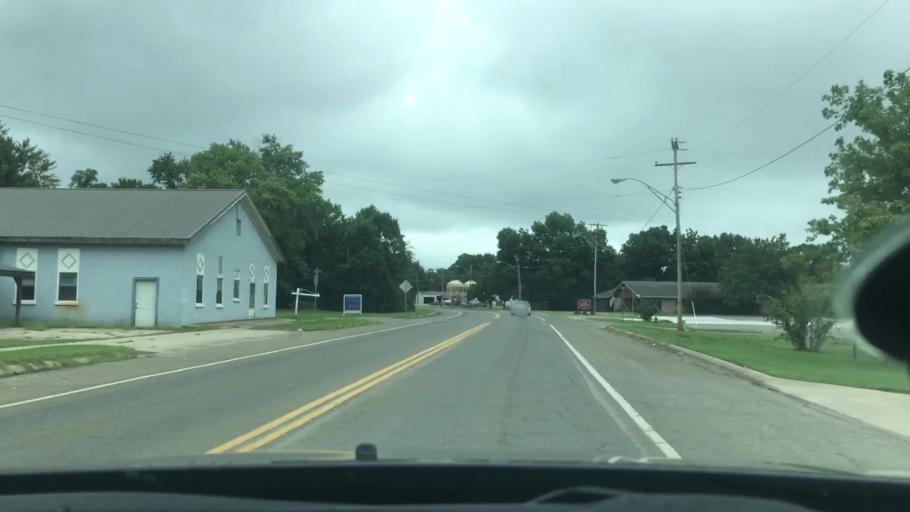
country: US
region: Oklahoma
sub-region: Sequoyah County
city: Vian
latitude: 35.4999
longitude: -94.9690
